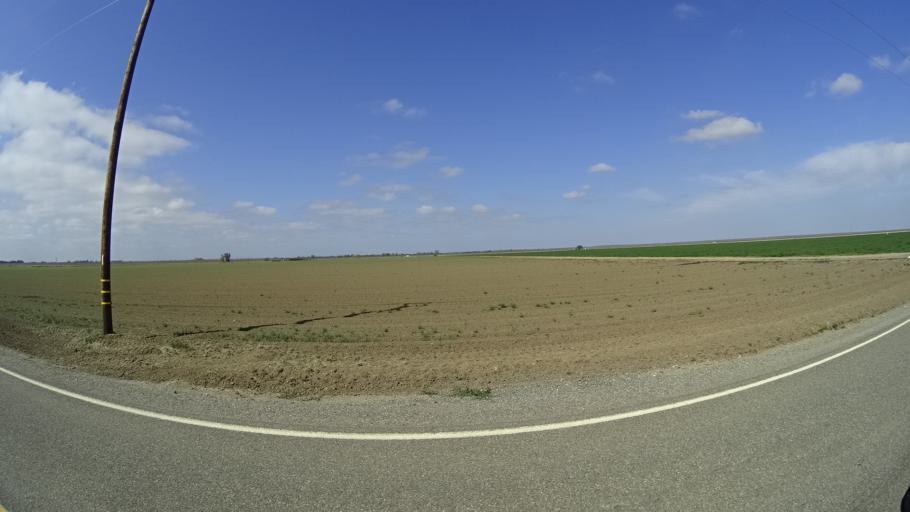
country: US
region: California
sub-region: Butte County
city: Biggs
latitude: 39.4236
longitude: -121.9295
